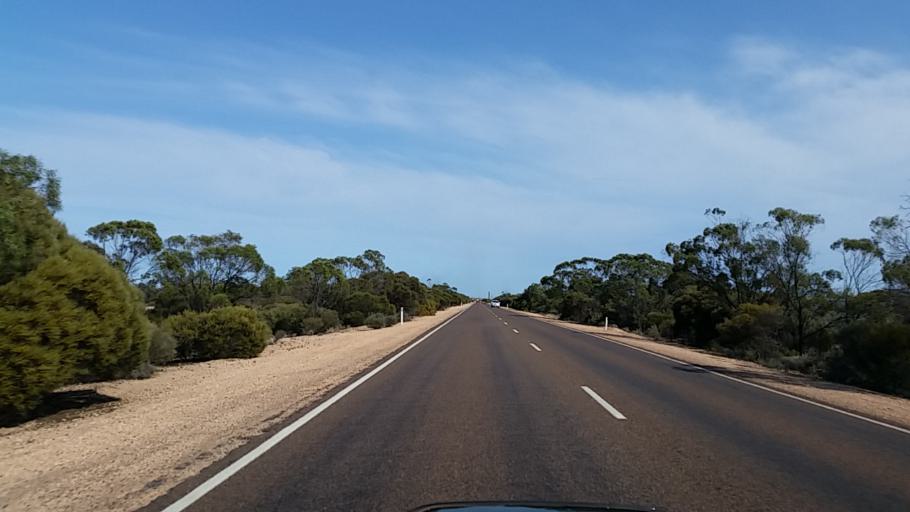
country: AU
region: South Australia
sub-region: Whyalla
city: Whyalla
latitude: -32.9563
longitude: 137.5758
